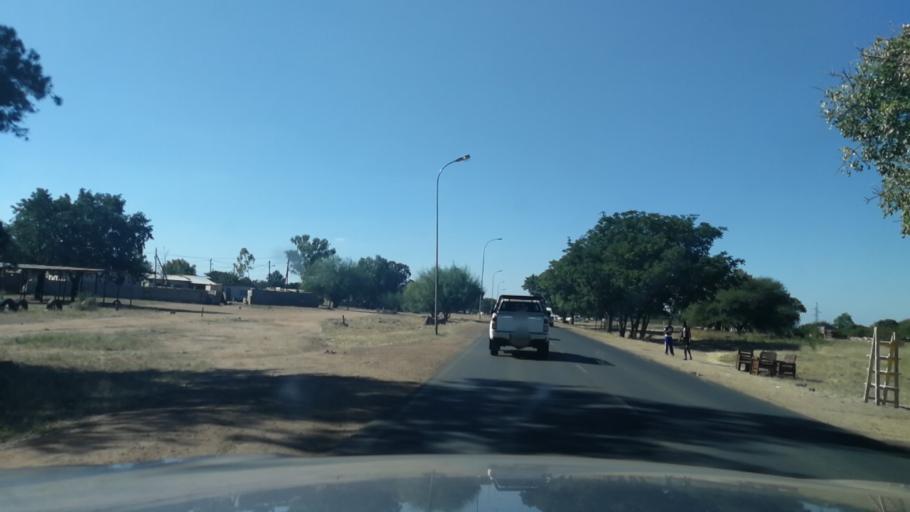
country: BW
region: South East
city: Gaborone
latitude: -24.6906
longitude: 25.9004
